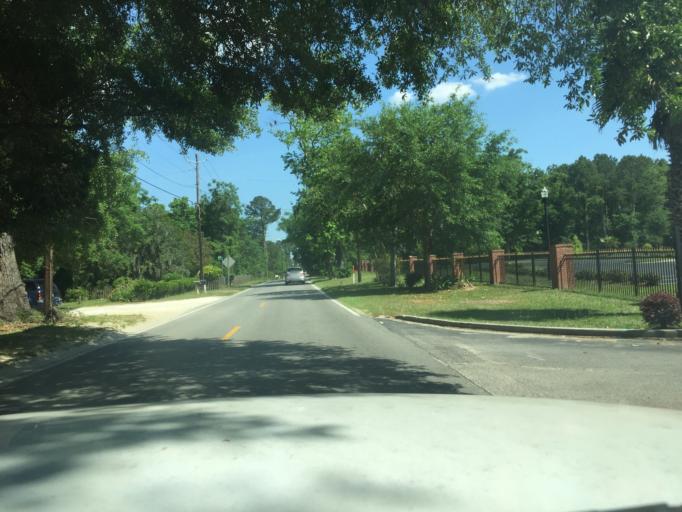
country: US
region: Georgia
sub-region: Chatham County
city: Georgetown
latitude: 32.0019
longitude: -81.2794
